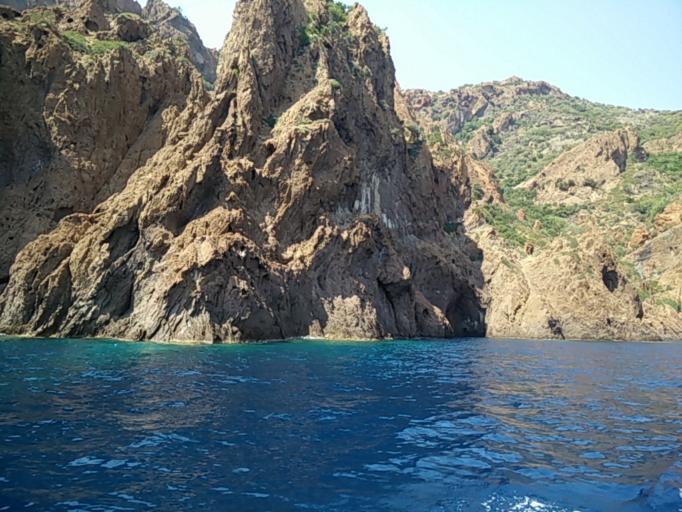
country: FR
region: Corsica
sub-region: Departement de la Corse-du-Sud
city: Cargese
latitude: 42.3356
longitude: 8.5679
